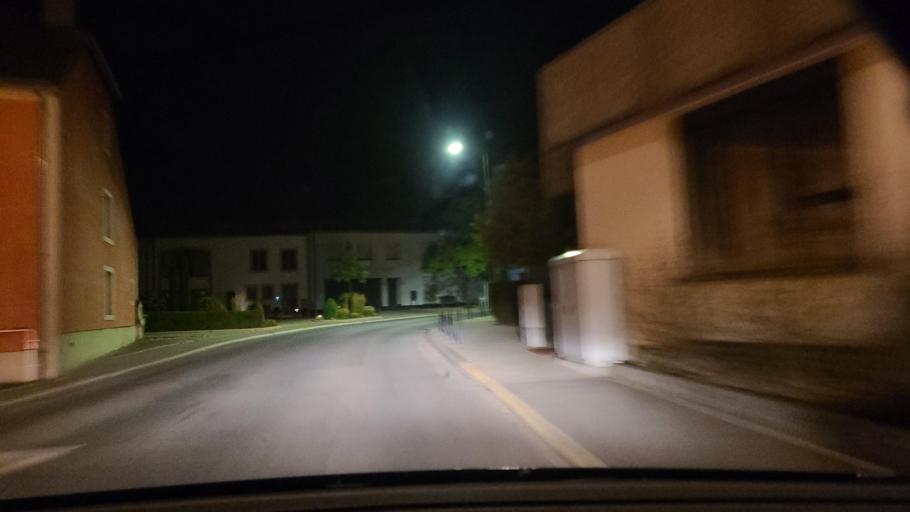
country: LU
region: Luxembourg
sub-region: Canton de Capellen
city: Bascharage
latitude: 49.5670
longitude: 5.9066
